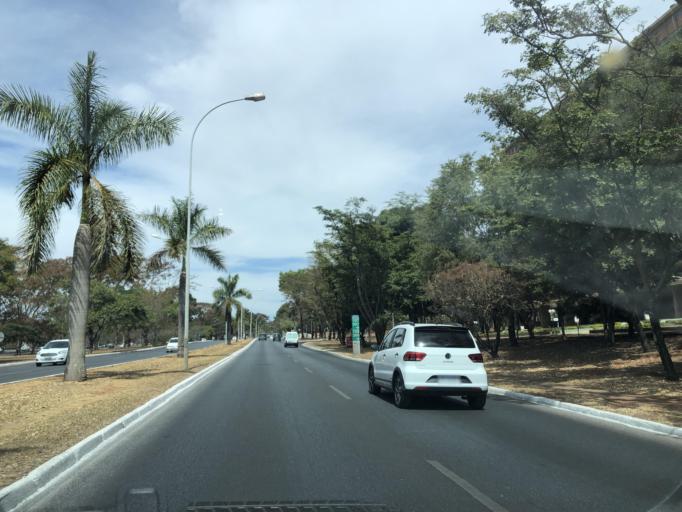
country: BR
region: Federal District
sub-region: Brasilia
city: Brasilia
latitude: -15.7623
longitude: -47.8858
